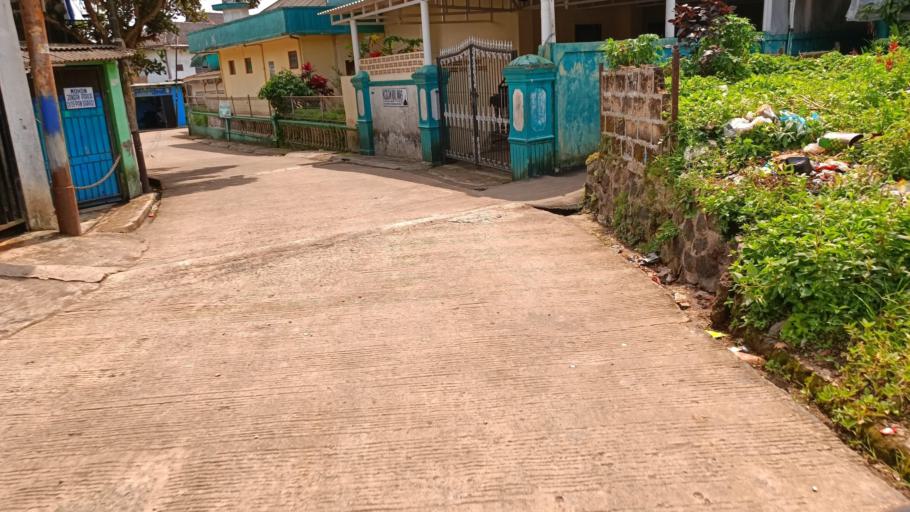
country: ID
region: West Java
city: Caringin
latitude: -6.6530
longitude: 106.8921
